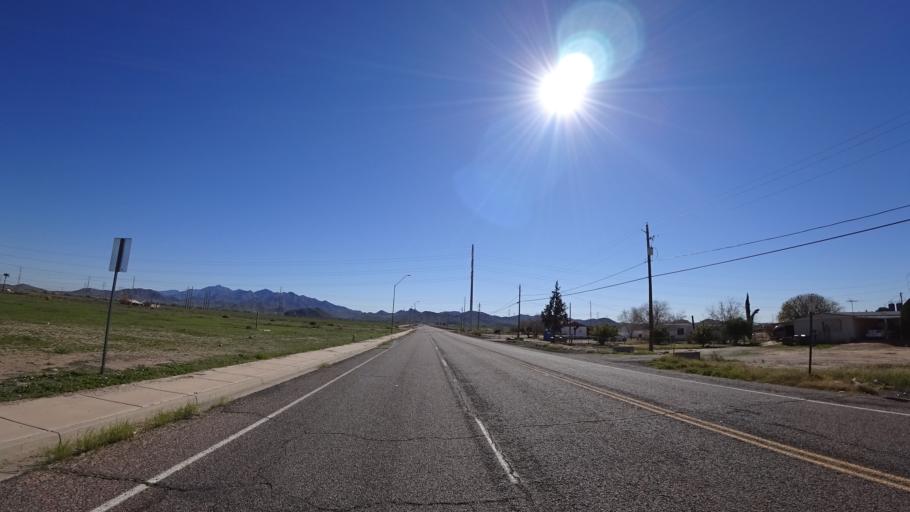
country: US
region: Arizona
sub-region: Maricopa County
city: Goodyear
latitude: 33.4080
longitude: -112.3751
